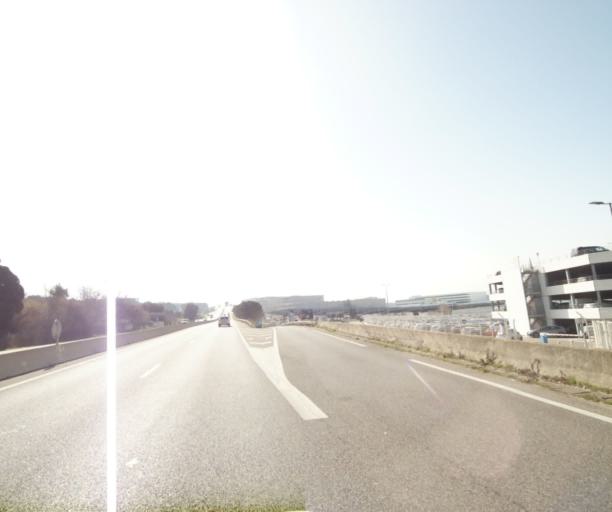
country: FR
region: Provence-Alpes-Cote d'Azur
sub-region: Departement des Bouches-du-Rhone
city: Saint-Victoret
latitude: 43.4364
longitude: 5.2352
